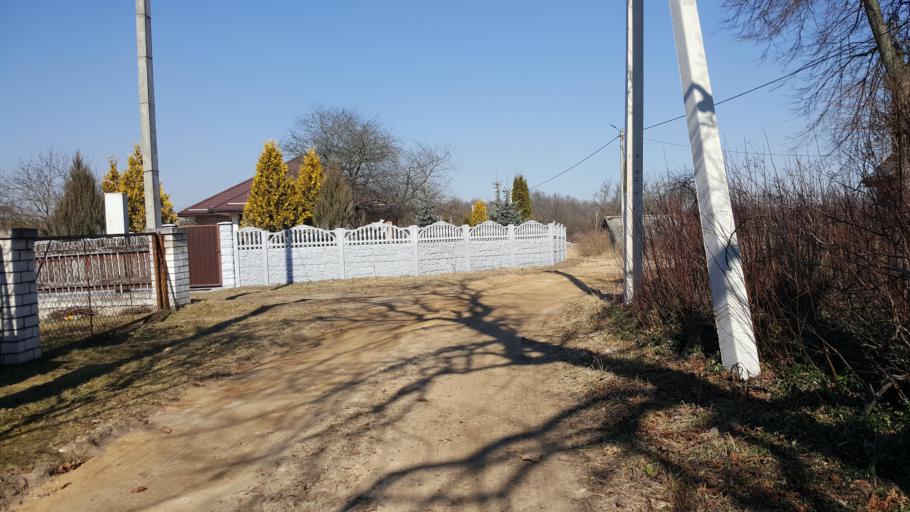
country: BY
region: Brest
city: Kamyanyets
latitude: 52.3622
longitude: 23.7631
